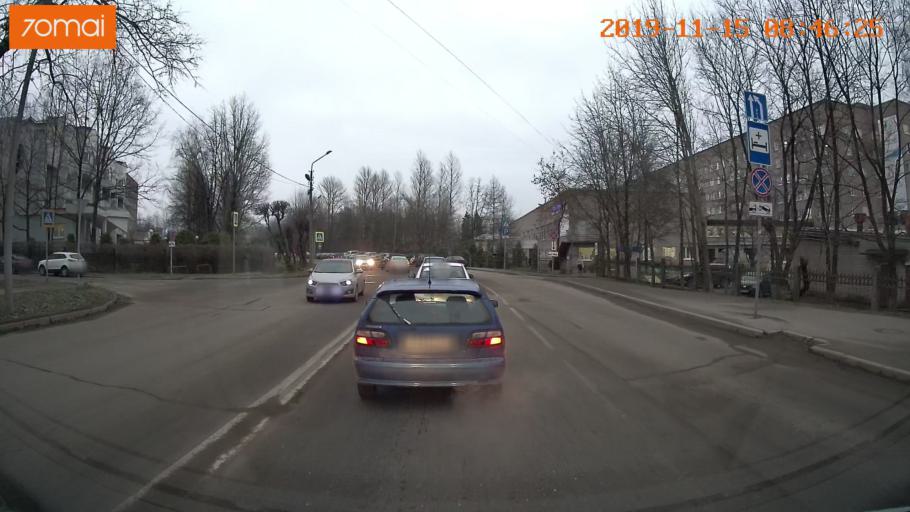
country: RU
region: Vologda
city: Cherepovets
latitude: 59.1187
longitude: 37.9065
